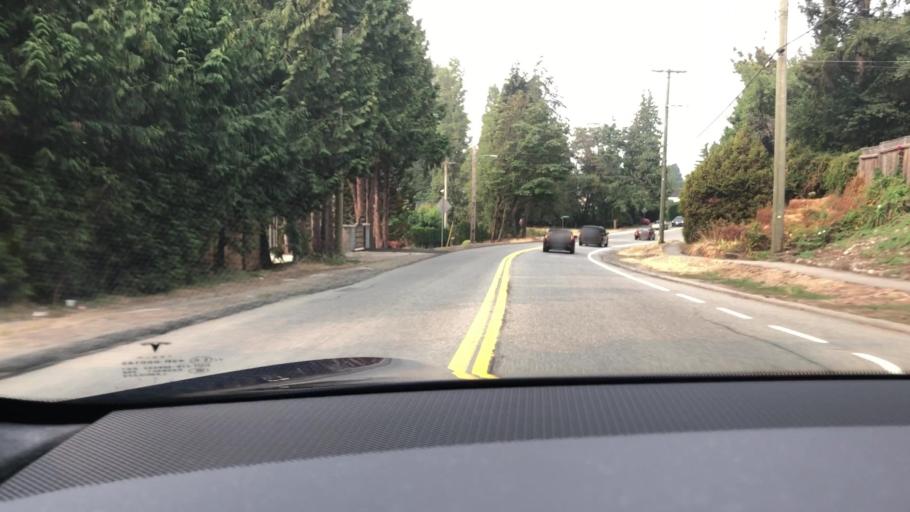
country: CA
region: British Columbia
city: Burnaby
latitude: 49.2090
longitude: -123.0140
